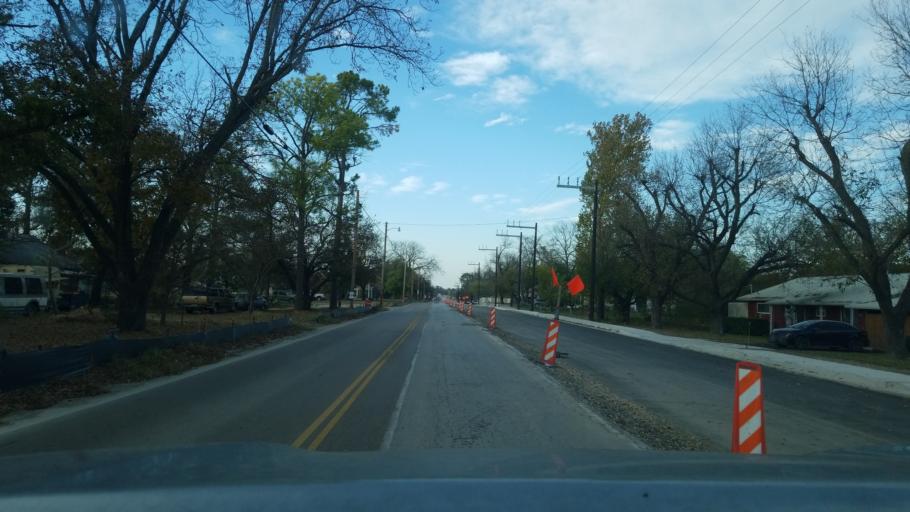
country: US
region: Texas
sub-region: Brown County
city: Lake Brownwood
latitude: 32.0890
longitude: -98.9641
